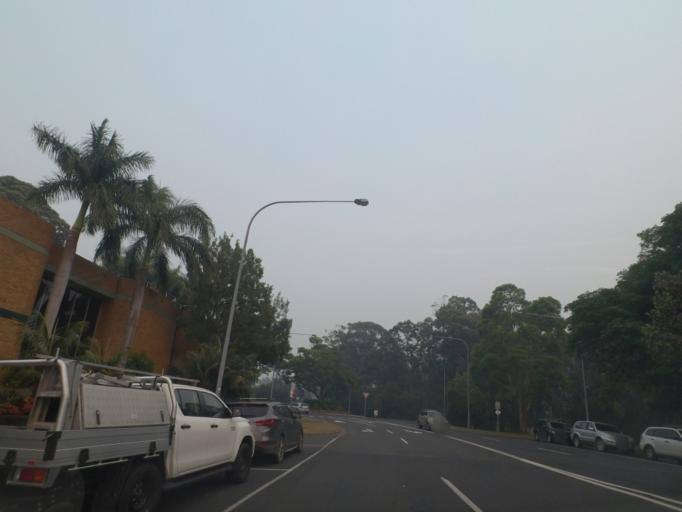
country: AU
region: New South Wales
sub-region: Coffs Harbour
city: Coffs Harbour
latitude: -30.2952
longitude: 153.1178
